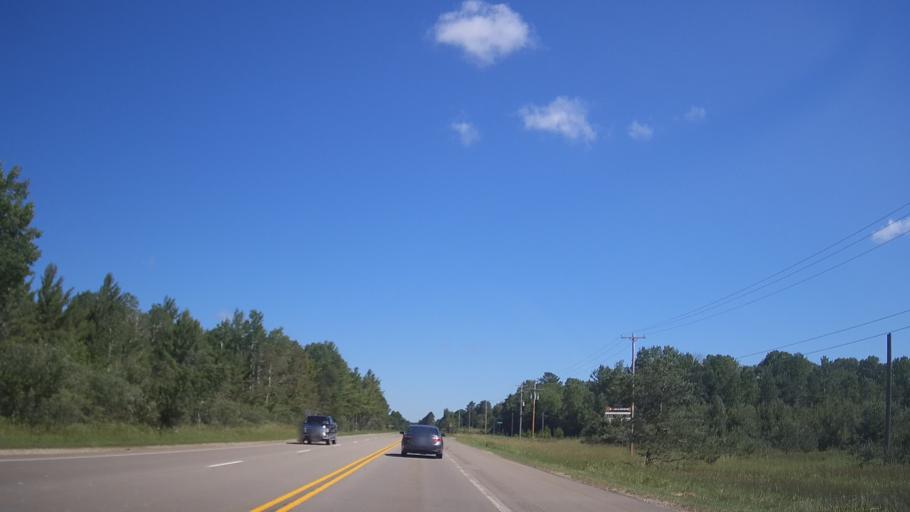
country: US
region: Michigan
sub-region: Cheboygan County
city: Indian River
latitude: 45.5275
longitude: -84.7818
